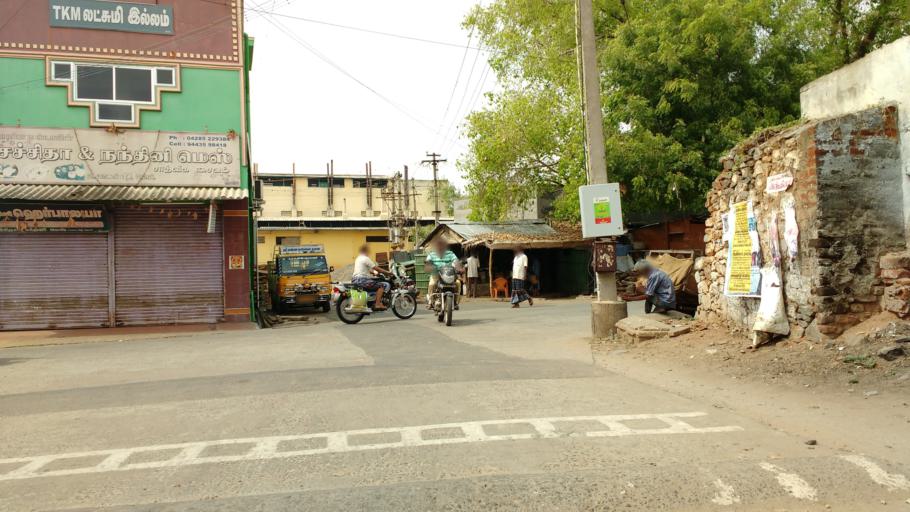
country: IN
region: Tamil Nadu
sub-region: Erode
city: Gobichettipalayam
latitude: 11.4579
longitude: 77.4330
